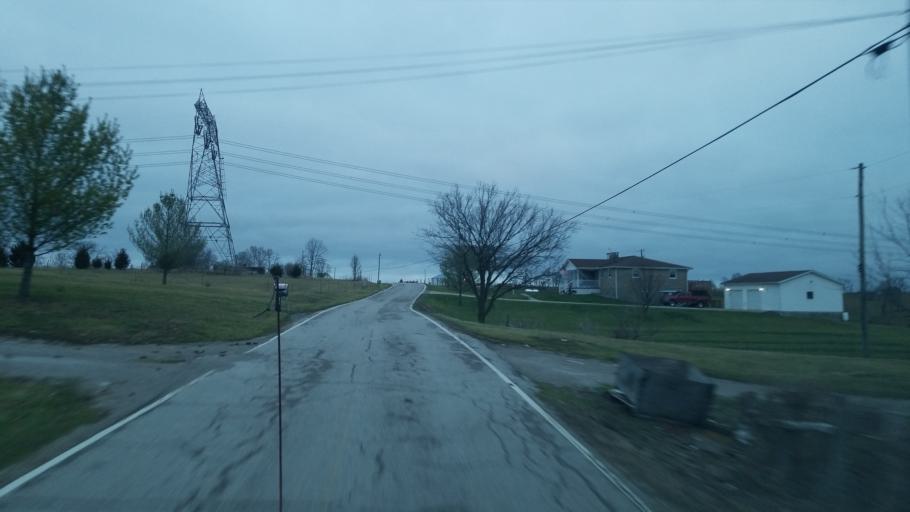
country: US
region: Kentucky
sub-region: Mason County
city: Maysville
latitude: 38.5560
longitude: -83.6897
